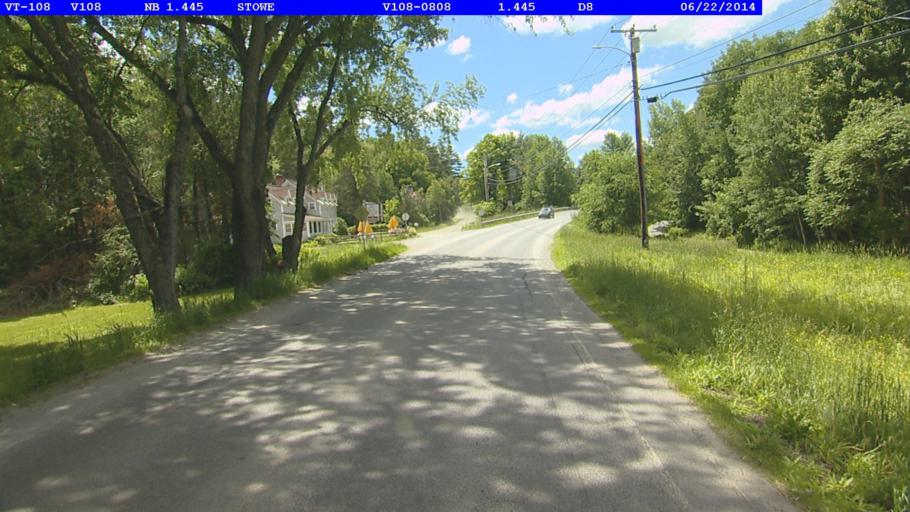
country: US
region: Vermont
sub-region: Lamoille County
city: Morristown
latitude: 44.4727
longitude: -72.7052
